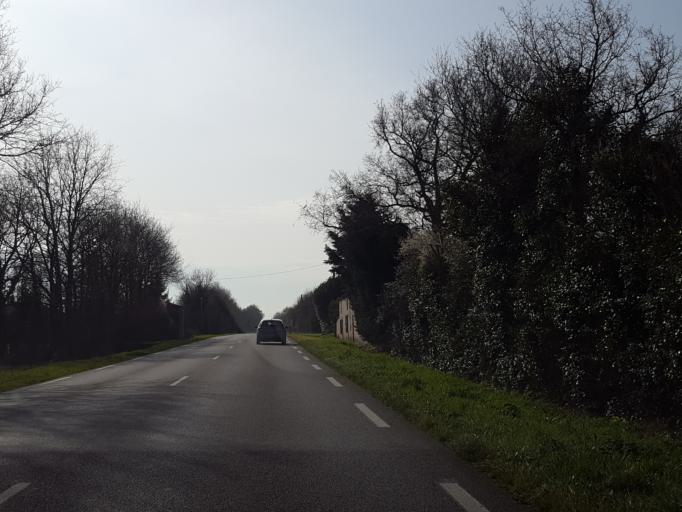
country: FR
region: Pays de la Loire
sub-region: Departement de la Vendee
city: Les Lucs-sur-Boulogne
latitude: 46.8263
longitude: -1.4763
